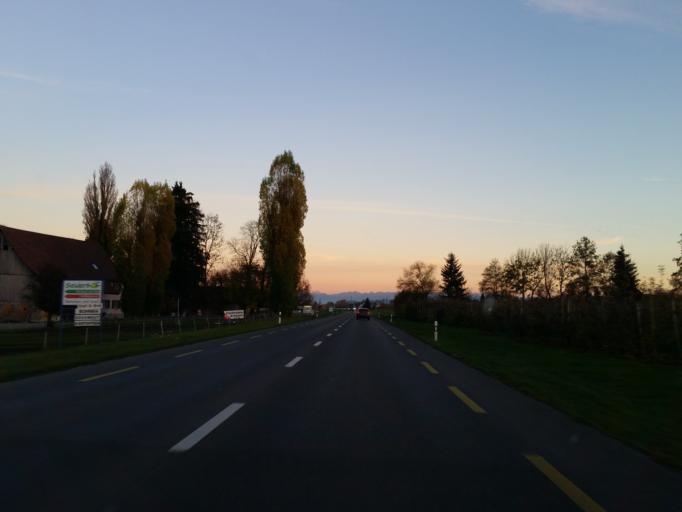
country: CH
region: Thurgau
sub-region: Kreuzlingen District
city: Guttingen
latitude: 47.6005
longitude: 9.2979
